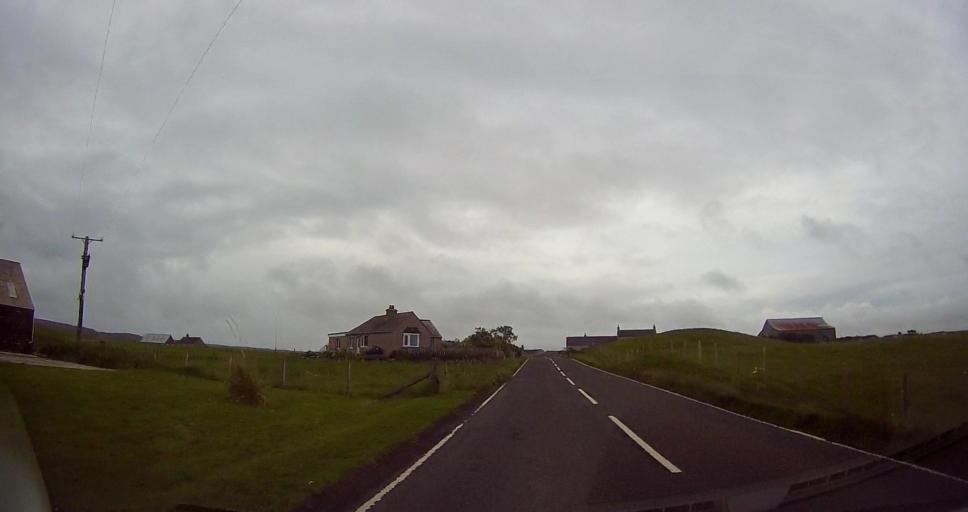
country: GB
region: Scotland
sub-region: Orkney Islands
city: Stromness
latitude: 59.0287
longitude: -3.1761
